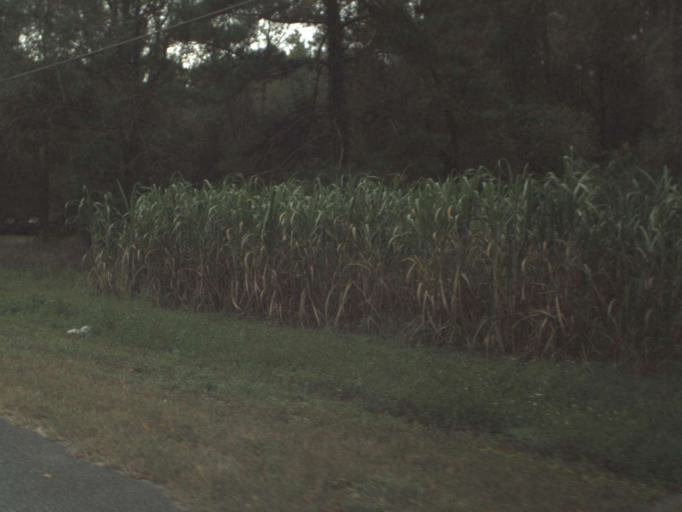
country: US
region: Florida
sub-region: Wakulla County
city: Crawfordville
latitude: 30.1301
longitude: -84.3879
